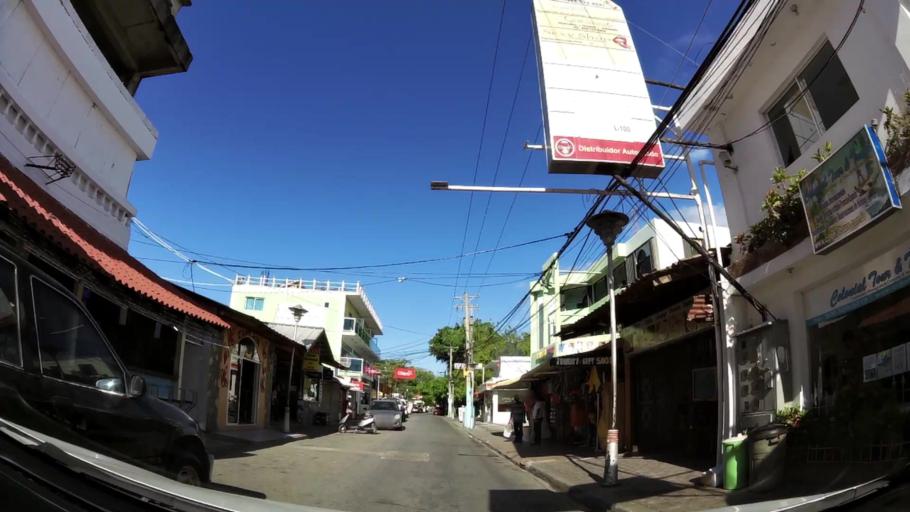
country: DO
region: Santo Domingo
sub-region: Santo Domingo
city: Boca Chica
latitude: 18.4478
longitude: -69.6089
